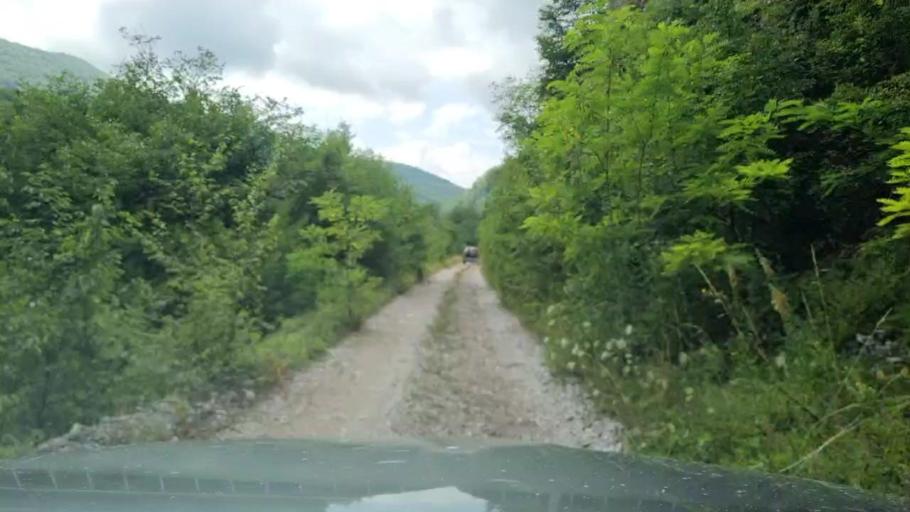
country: BA
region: Republika Srpska
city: Rogatica
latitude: 43.7645
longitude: 18.8697
